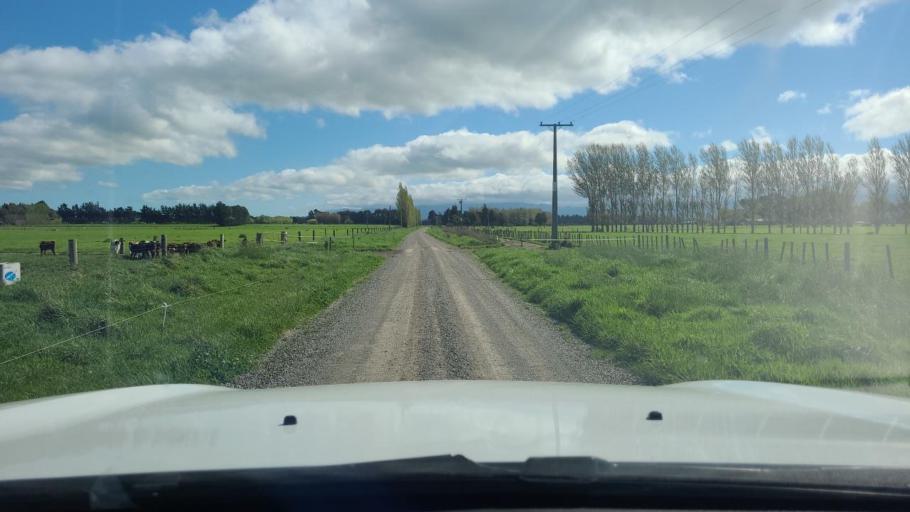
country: NZ
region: Wellington
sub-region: South Wairarapa District
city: Waipawa
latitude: -41.2505
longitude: 175.3570
